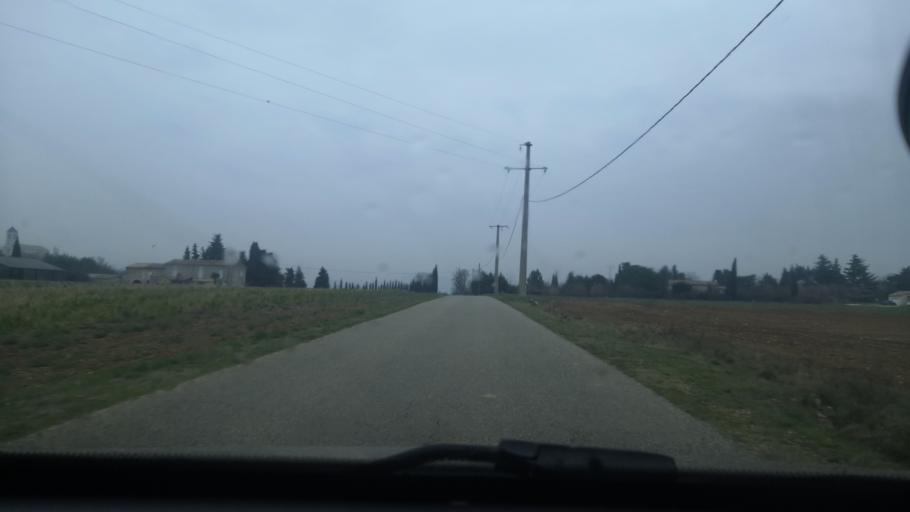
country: FR
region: Rhone-Alpes
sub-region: Departement de la Drome
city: Montboucher-sur-Jabron
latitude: 44.5510
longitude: 4.8126
